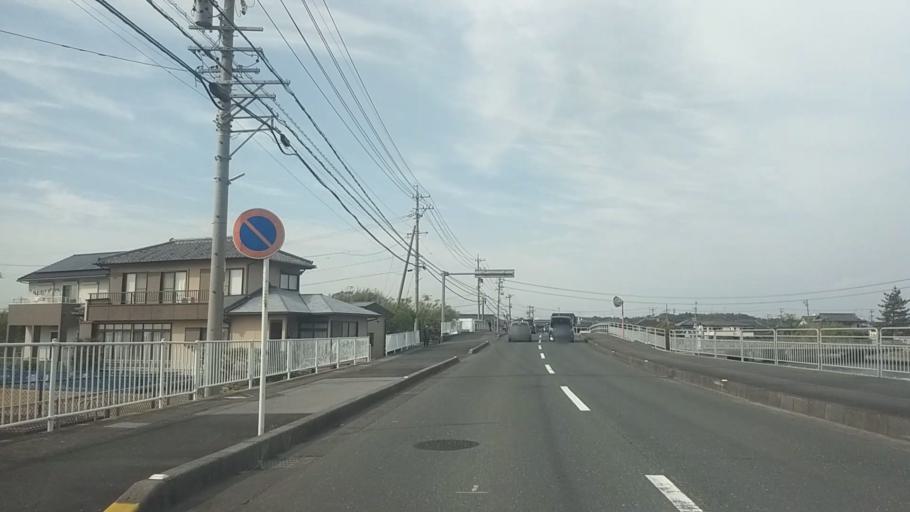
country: JP
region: Shizuoka
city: Kosai-shi
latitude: 34.7202
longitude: 137.5924
